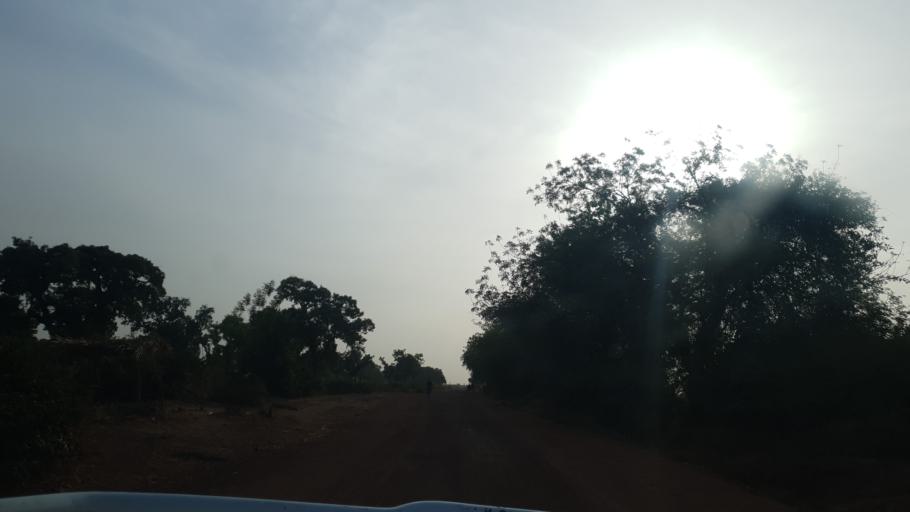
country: ML
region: Koulikoro
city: Dioila
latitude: 12.7704
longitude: -6.9309
